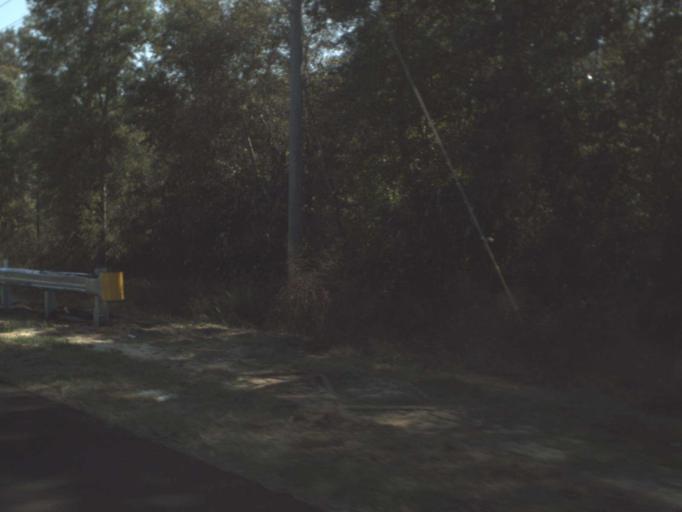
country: US
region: Florida
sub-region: Walton County
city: DeFuniak Springs
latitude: 30.8025
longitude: -86.1951
